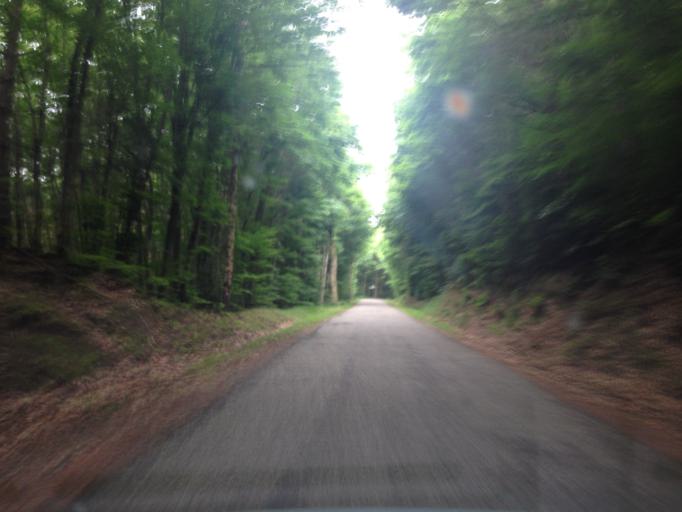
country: FR
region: Alsace
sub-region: Departement du Bas-Rhin
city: Neuwiller-les-Saverne
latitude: 48.8353
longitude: 7.3933
